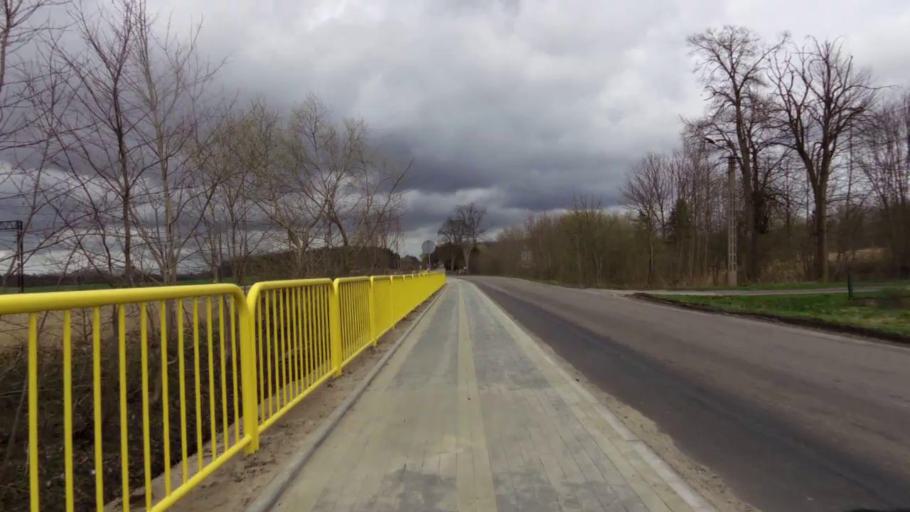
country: PL
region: West Pomeranian Voivodeship
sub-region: Powiat koszalinski
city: Sianow
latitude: 54.2506
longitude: 16.3068
